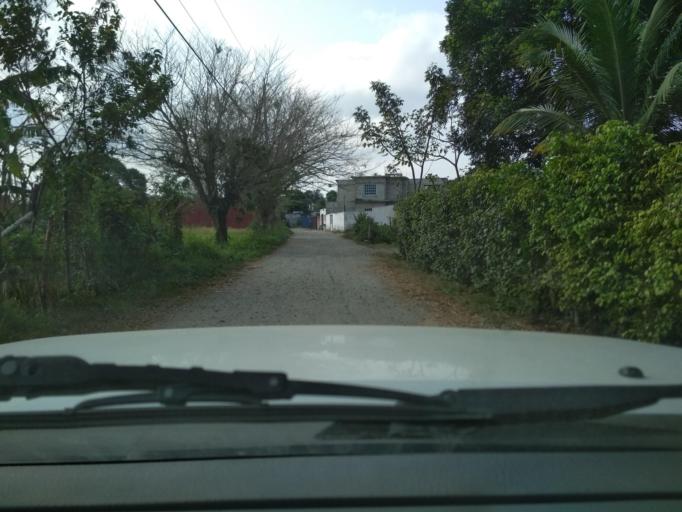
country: MX
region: Veracruz
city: El Tejar
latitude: 19.0811
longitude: -96.1633
